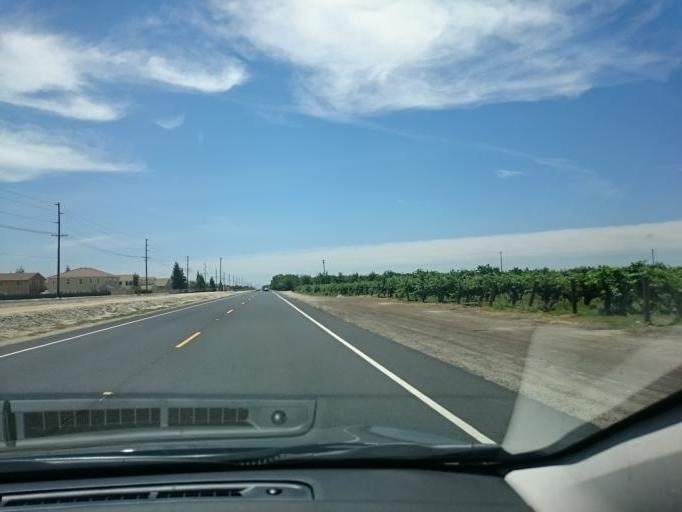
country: US
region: California
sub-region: Stanislaus County
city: Hughson
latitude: 37.6092
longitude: -120.8546
